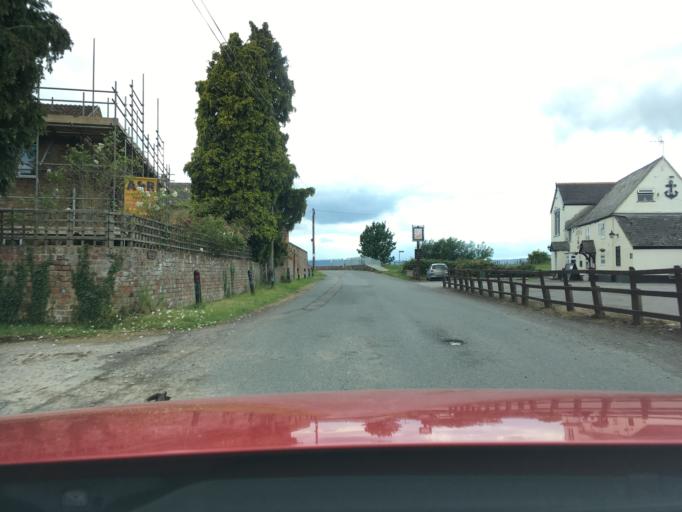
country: GB
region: England
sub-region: Gloucestershire
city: Stonehouse
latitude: 51.7971
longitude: -2.3468
